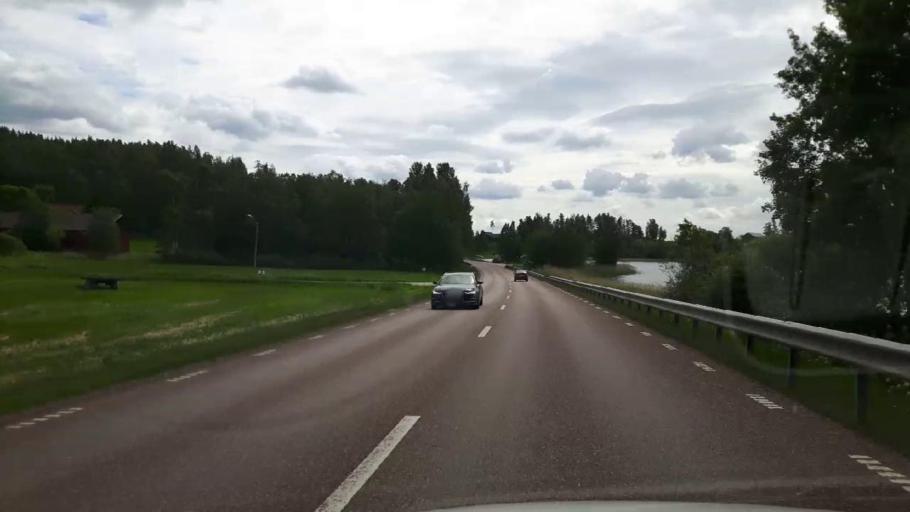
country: SE
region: Dalarna
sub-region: Hedemora Kommun
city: Hedemora
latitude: 60.3254
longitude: 15.9513
